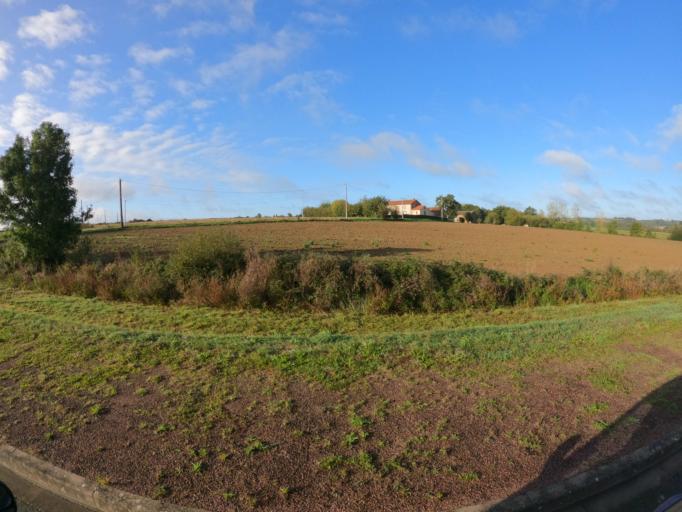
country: FR
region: Pays de la Loire
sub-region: Departement de Maine-et-Loire
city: La Seguiniere
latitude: 47.0565
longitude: -0.9449
